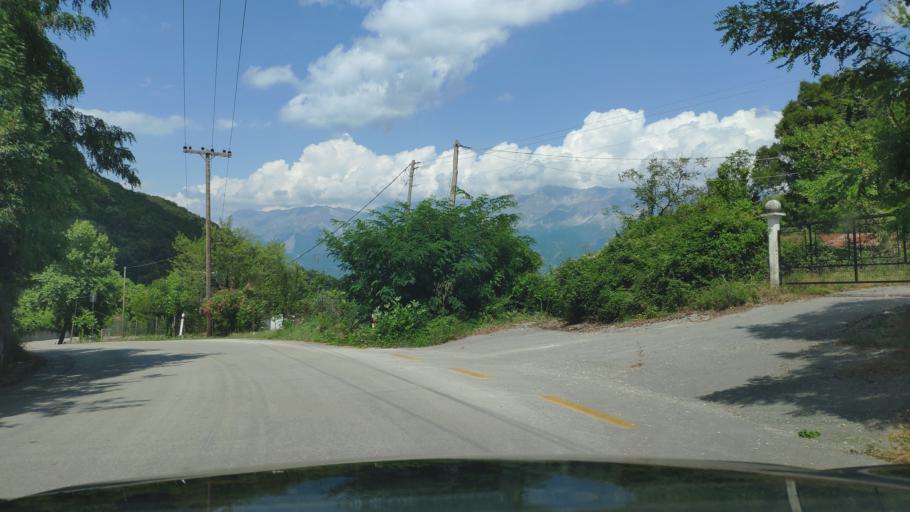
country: GR
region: Epirus
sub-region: Nomos Artas
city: Agios Dimitrios
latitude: 39.3512
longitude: 21.0153
